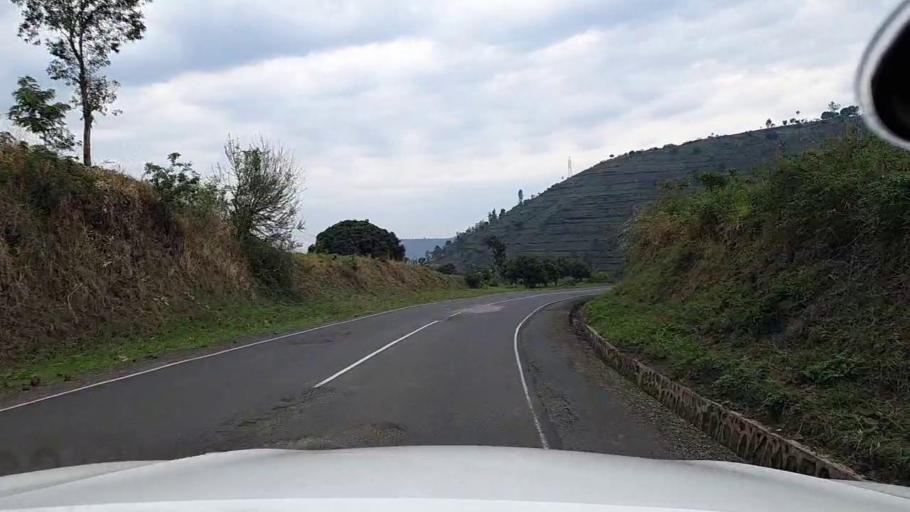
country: RW
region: Western Province
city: Cyangugu
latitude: -2.6723
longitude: 29.0038
